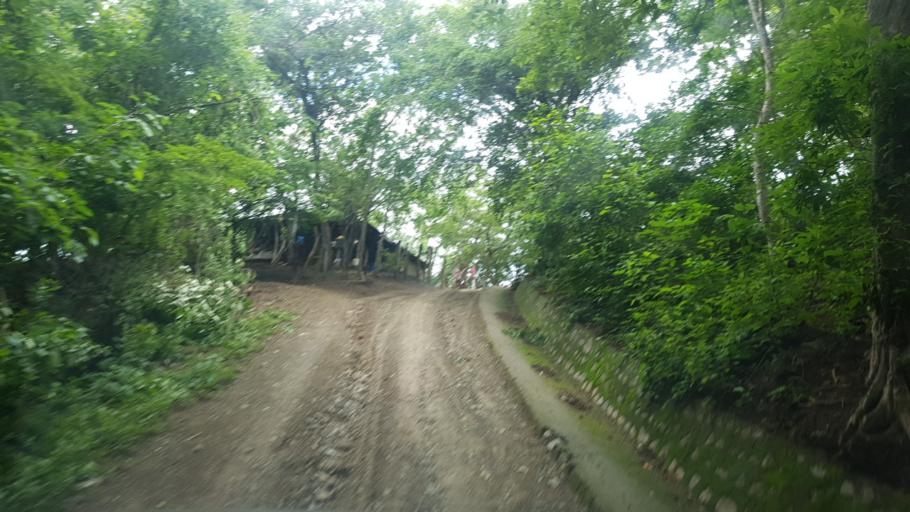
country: NI
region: Nueva Segovia
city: Mozonte
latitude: 13.5868
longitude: -86.3970
